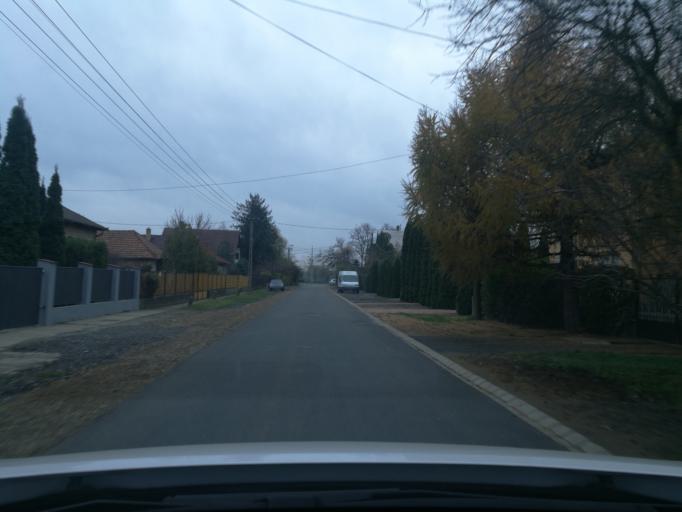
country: HU
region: Szabolcs-Szatmar-Bereg
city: Nyirpazony
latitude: 47.9511
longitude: 21.7823
